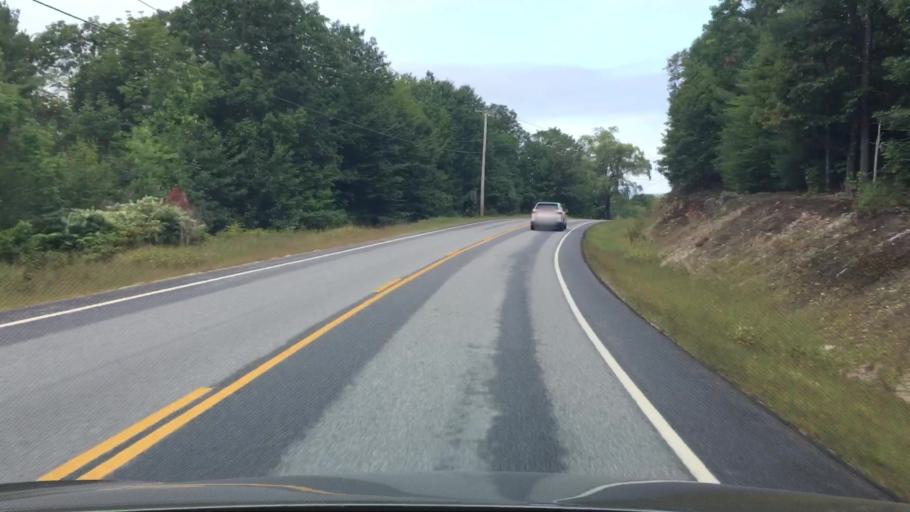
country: US
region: Maine
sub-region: Oxford County
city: Hartford
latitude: 44.3637
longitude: -70.3155
